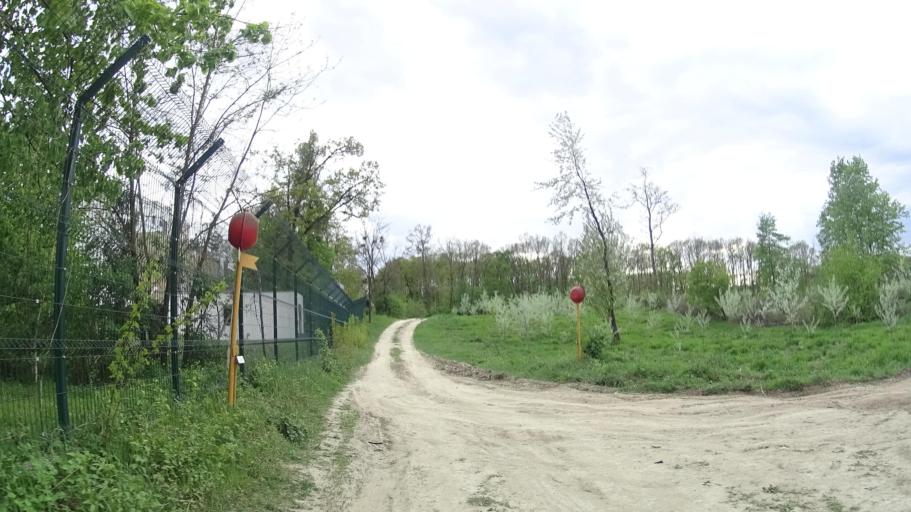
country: HU
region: Pest
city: Szada
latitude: 47.6063
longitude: 19.3234
